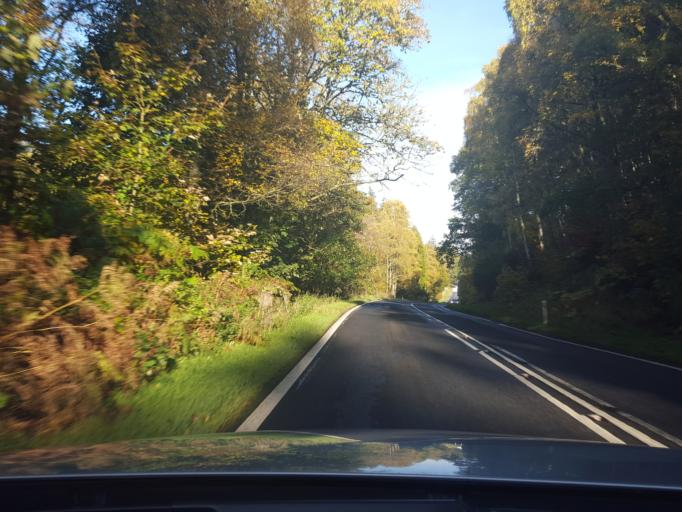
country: GB
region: Scotland
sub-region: Highland
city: Inverness
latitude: 57.4394
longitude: -4.2987
